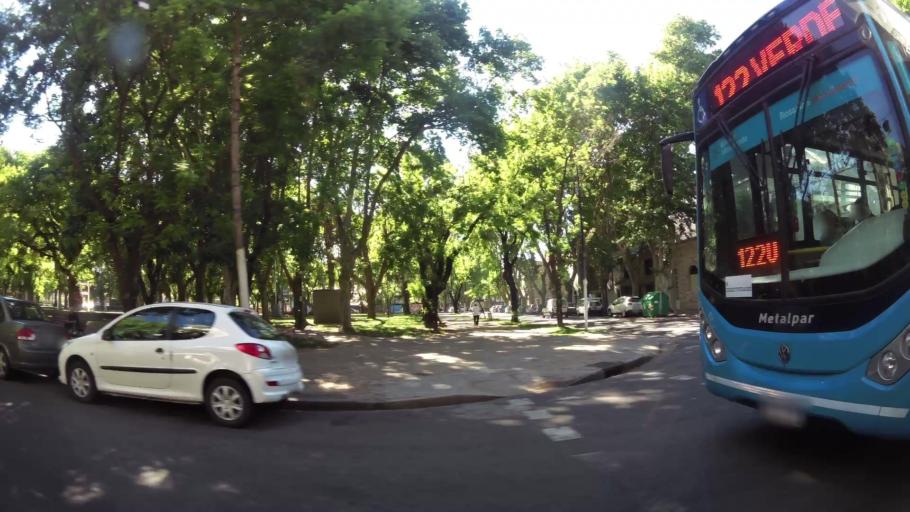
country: AR
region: Santa Fe
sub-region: Departamento de Rosario
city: Rosario
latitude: -32.9476
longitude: -60.6742
